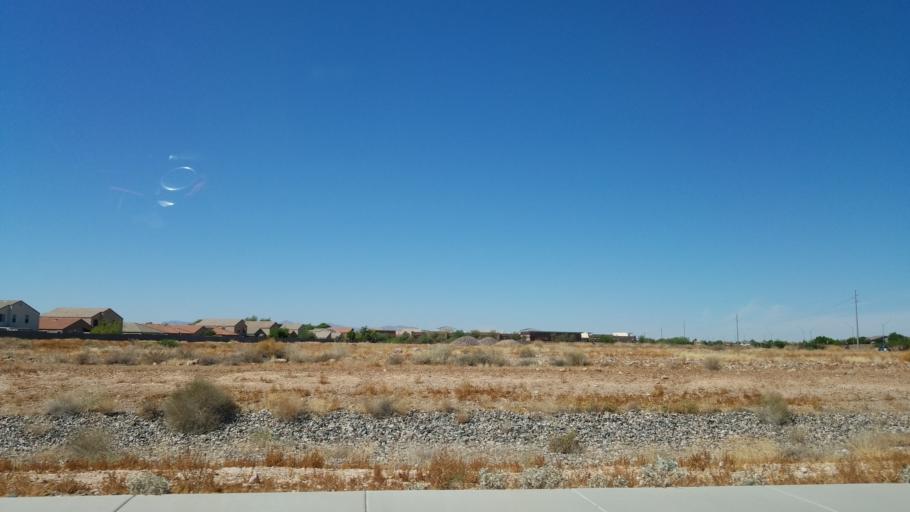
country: US
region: Arizona
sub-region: Maricopa County
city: Sun City West
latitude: 33.6808
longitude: -112.2701
